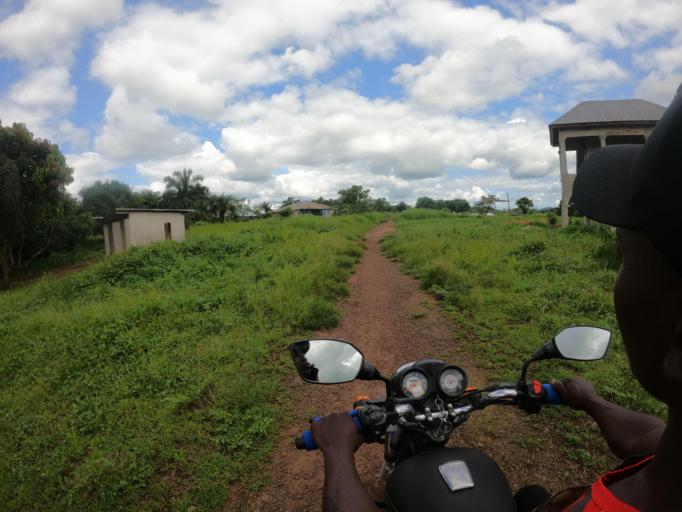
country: SL
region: Northern Province
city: Kamakwie
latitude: 9.5032
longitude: -12.2345
